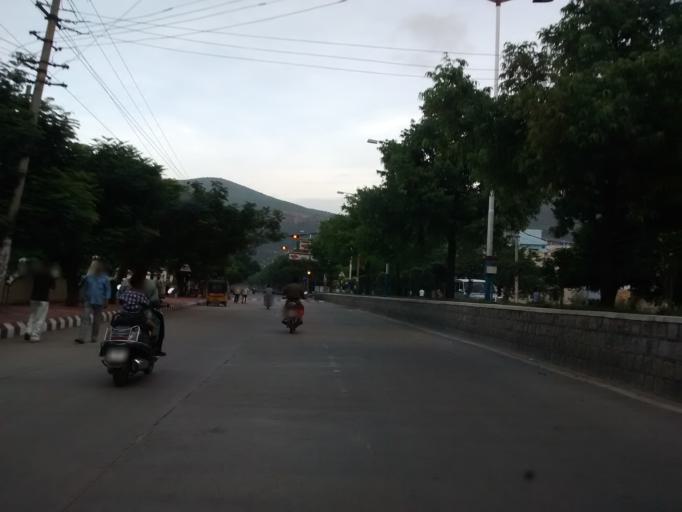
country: IN
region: Andhra Pradesh
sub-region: Chittoor
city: Akkarampalle
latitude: 13.6470
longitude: 79.4266
